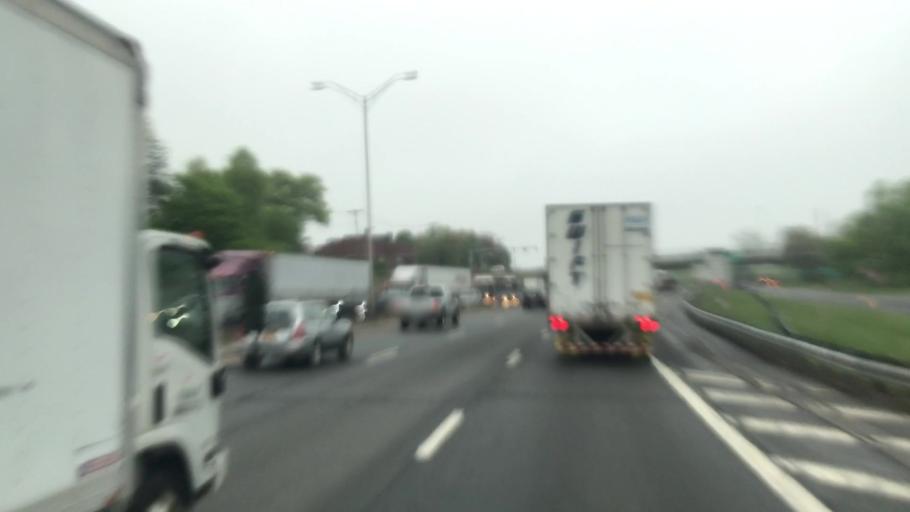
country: US
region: New York
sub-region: Westchester County
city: Yonkers
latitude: 40.9109
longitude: -73.8766
